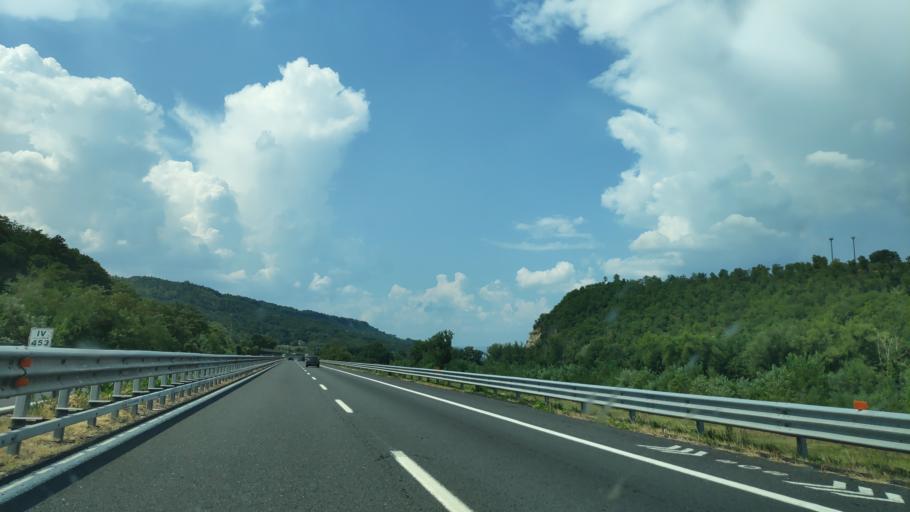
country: IT
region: Umbria
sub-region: Provincia di Terni
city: Orvieto Scalo
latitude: 42.7025
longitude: 12.1705
